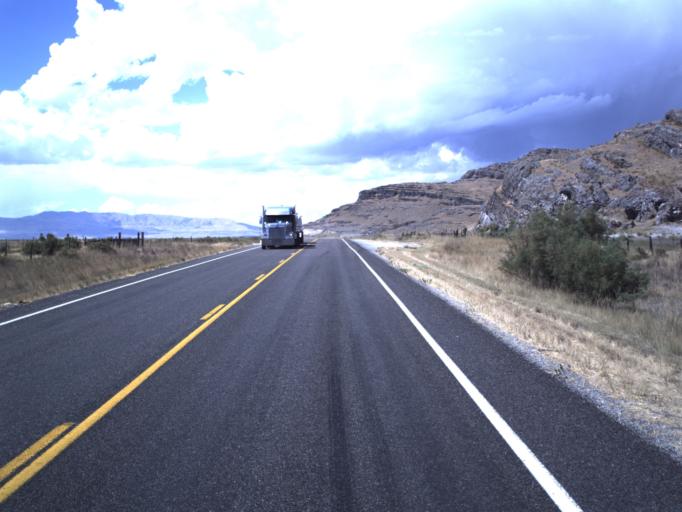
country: US
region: Utah
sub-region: Box Elder County
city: Elwood
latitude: 41.5763
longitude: -112.2322
